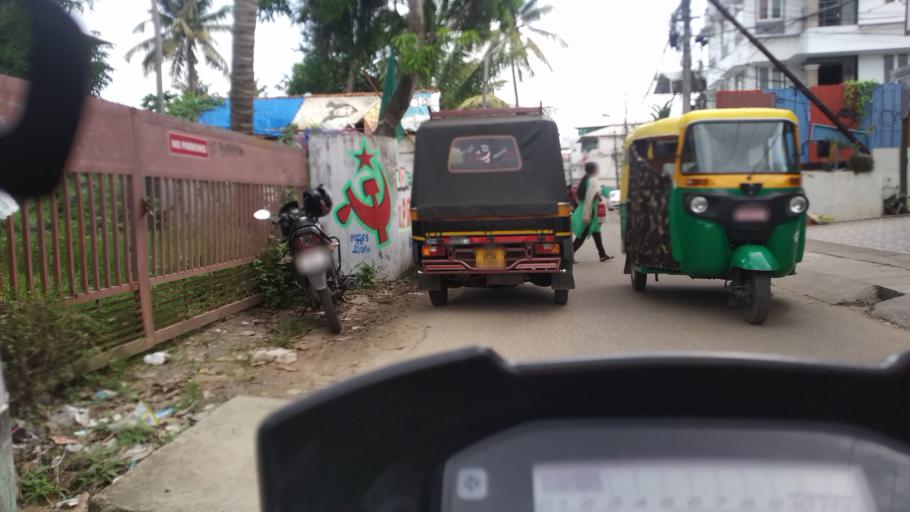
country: IN
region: Kerala
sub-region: Ernakulam
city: Cochin
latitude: 9.9851
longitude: 76.2939
